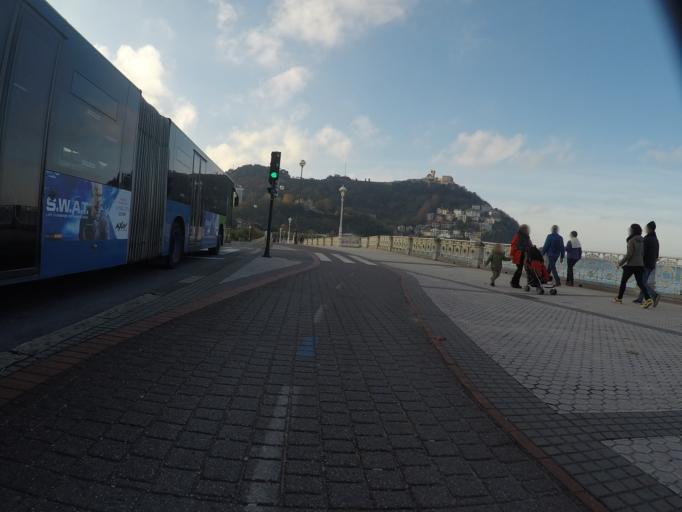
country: ES
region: Basque Country
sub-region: Provincia de Guipuzcoa
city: San Sebastian
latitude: 43.3155
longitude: -1.9991
